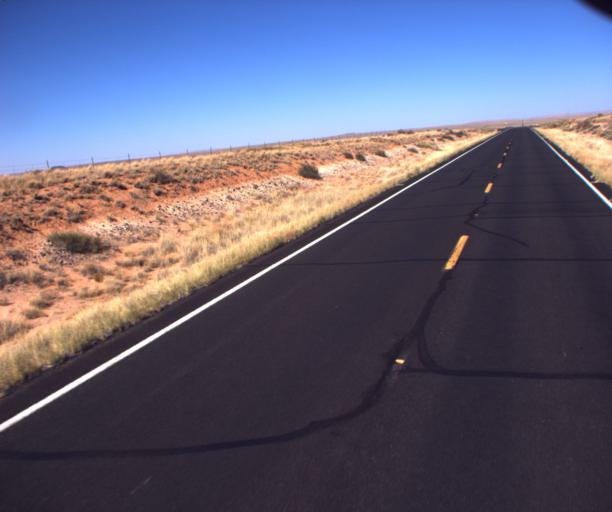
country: US
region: Arizona
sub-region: Navajo County
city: Dilkon
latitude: 35.5480
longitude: -110.4519
